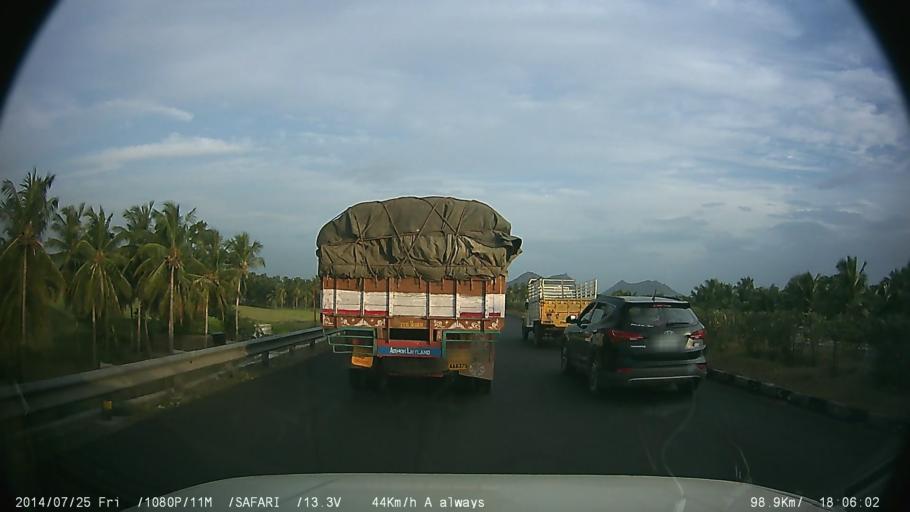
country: IN
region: Tamil Nadu
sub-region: Krishnagiri
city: Kaverippattanam
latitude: 12.4324
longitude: 78.2240
